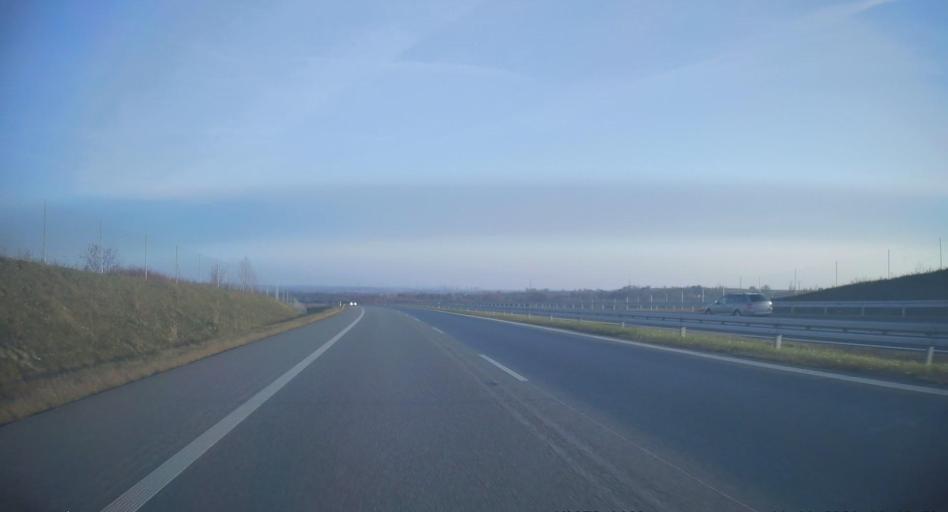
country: PL
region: Silesian Voivodeship
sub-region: Powiat bedzinski
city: Mierzecice
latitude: 50.4280
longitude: 19.1571
